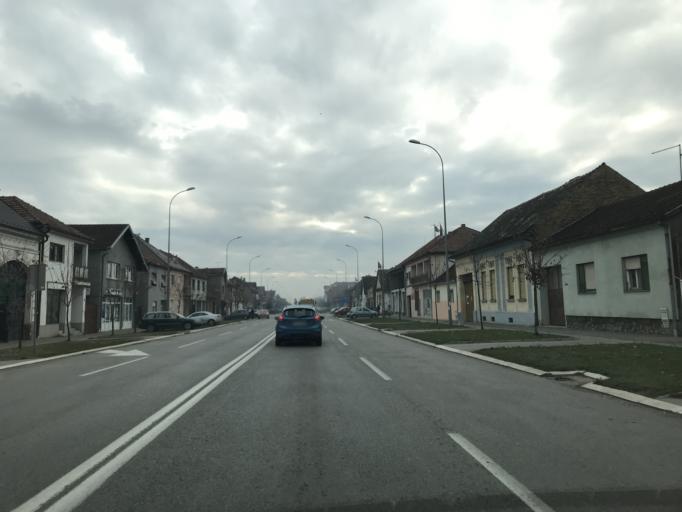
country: RS
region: Autonomna Pokrajina Vojvodina
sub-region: Sremski Okrug
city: Ingija
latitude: 45.0450
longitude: 20.0837
